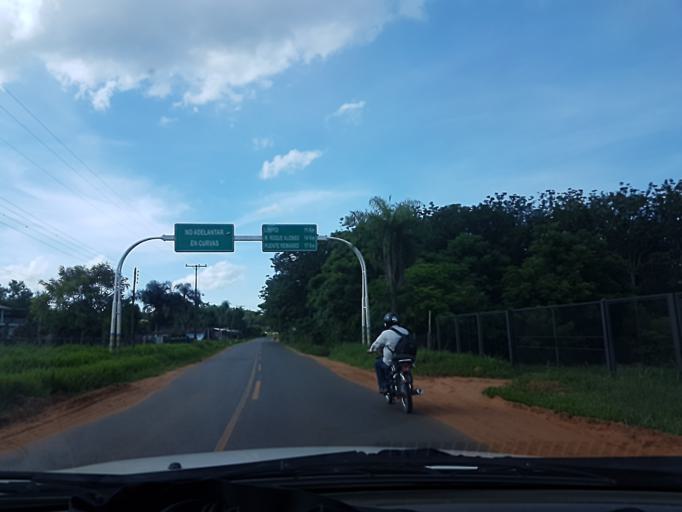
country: PY
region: Central
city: Limpio
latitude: -25.2299
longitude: -57.4488
